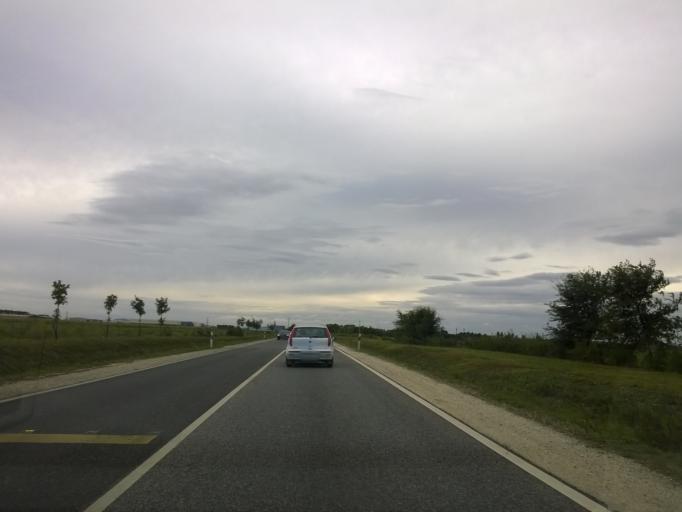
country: HU
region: Pest
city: Szigetszentmiklos
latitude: 47.3697
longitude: 19.0318
